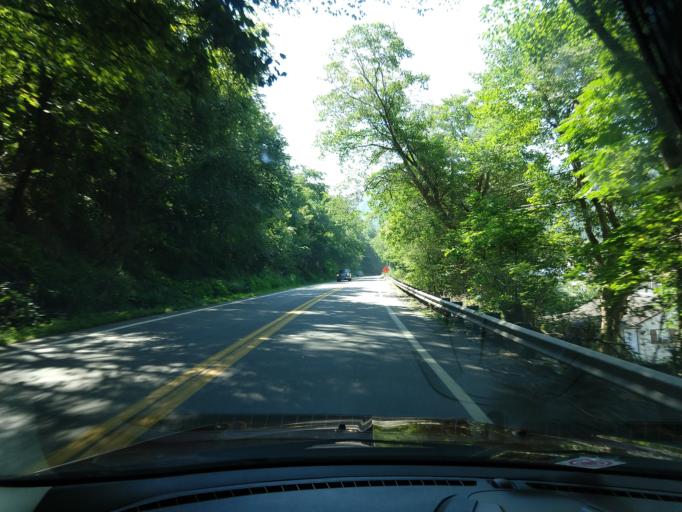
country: US
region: West Virginia
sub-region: Kanawha County
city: Montgomery
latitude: 38.1656
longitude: -81.3032
